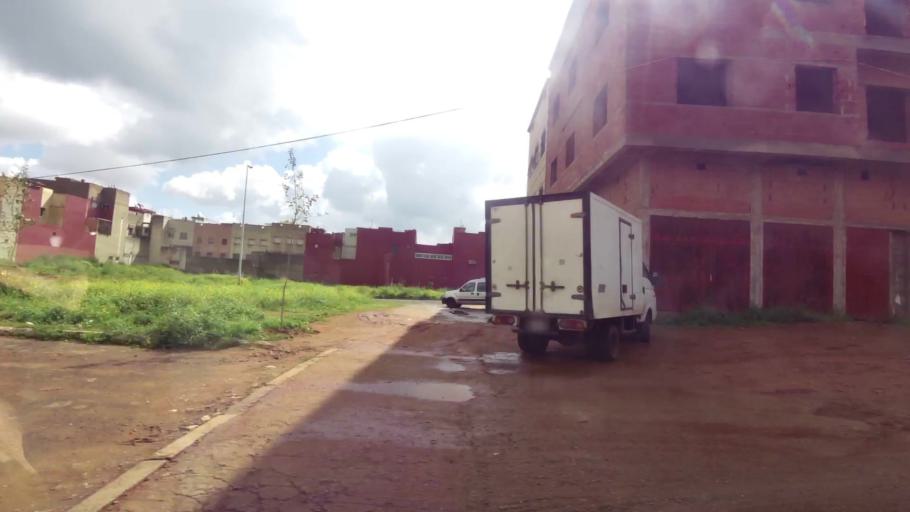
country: MA
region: Grand Casablanca
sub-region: Nouaceur
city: Bouskoura
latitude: 33.5096
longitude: -7.6507
